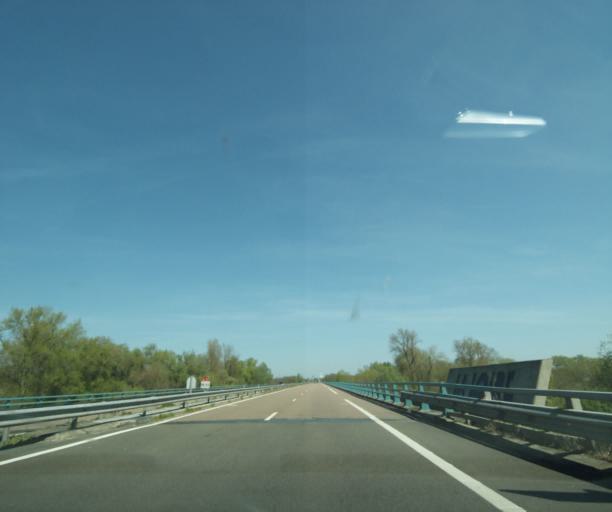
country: FR
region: Bourgogne
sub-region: Departement de la Nievre
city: Sermoise-sur-Loire
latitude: 46.9726
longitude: 3.1954
